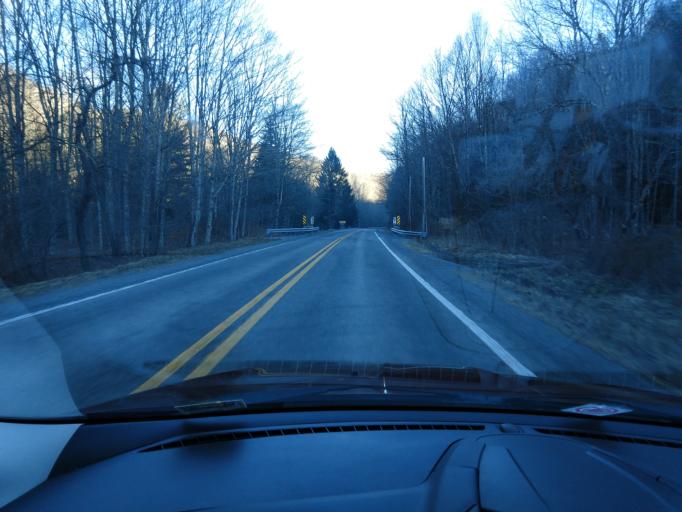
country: US
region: Virginia
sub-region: Highland County
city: Monterey
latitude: 38.5204
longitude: -79.7269
